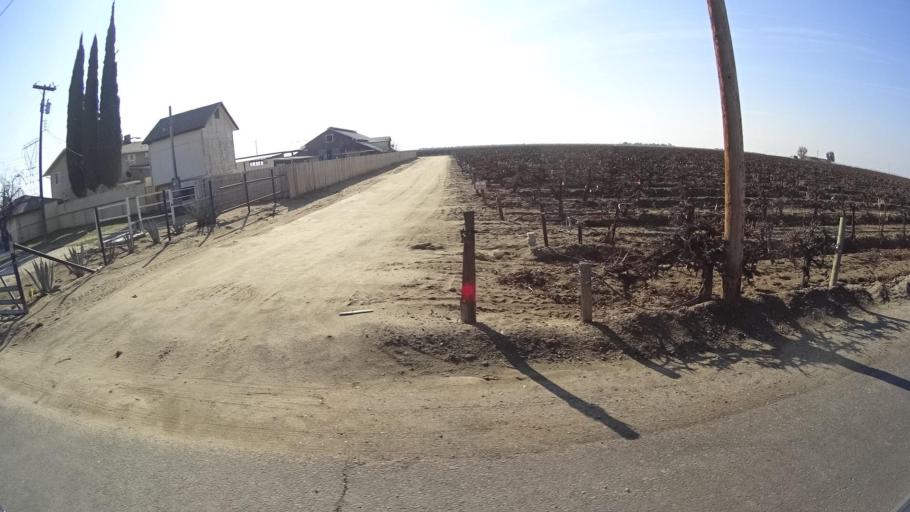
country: US
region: California
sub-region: Kern County
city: Weedpatch
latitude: 35.2378
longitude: -118.9242
